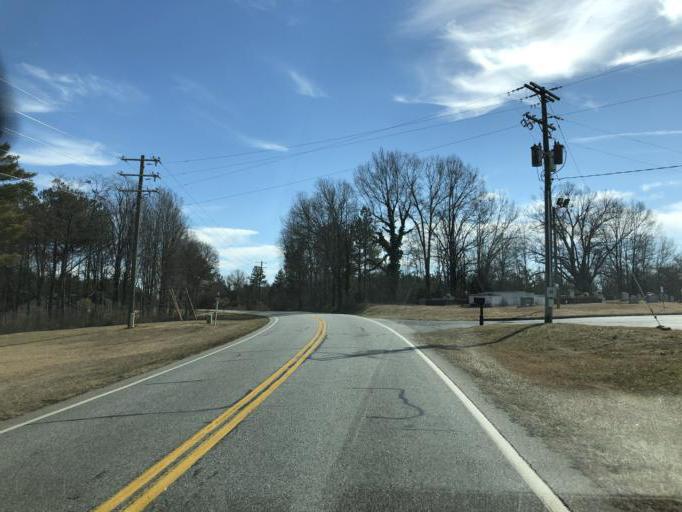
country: US
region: South Carolina
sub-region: Spartanburg County
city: Boiling Springs
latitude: 35.0545
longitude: -81.9353
